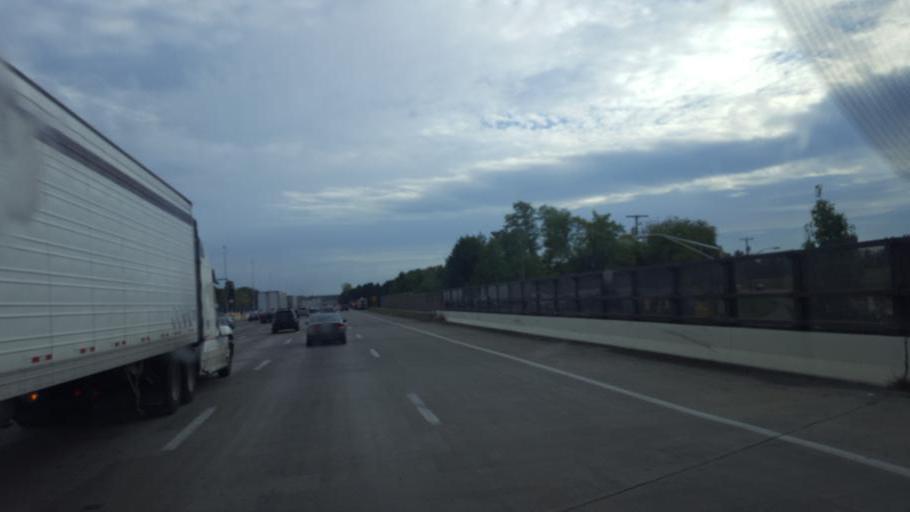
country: US
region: Ohio
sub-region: Franklin County
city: Westerville
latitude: 40.1344
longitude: -82.9718
